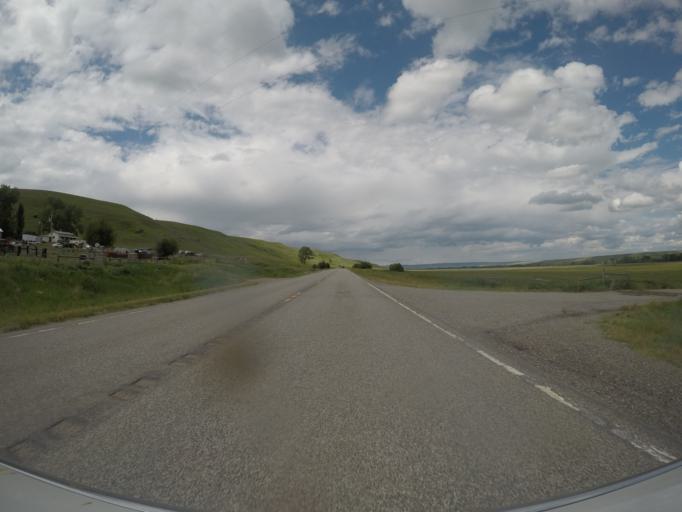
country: US
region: Montana
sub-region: Sweet Grass County
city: Big Timber
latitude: 45.7785
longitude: -109.9861
